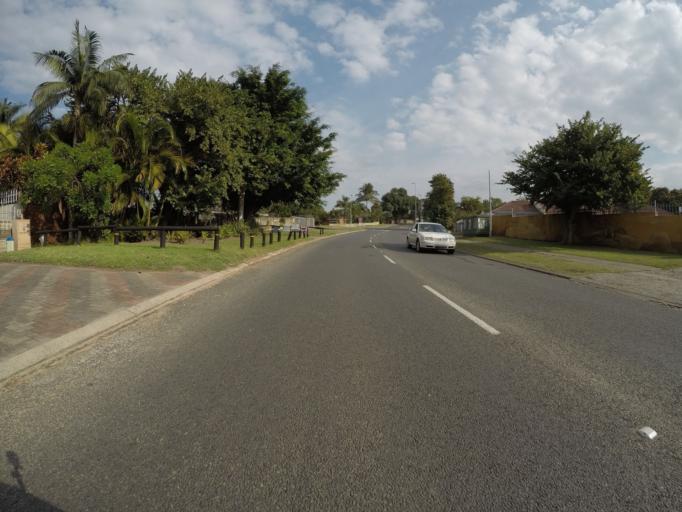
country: ZA
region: KwaZulu-Natal
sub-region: uThungulu District Municipality
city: Richards Bay
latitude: -28.7406
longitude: 32.0644
